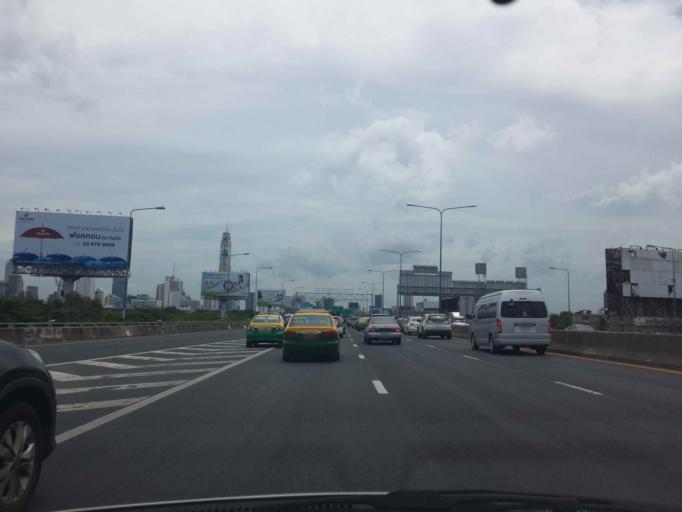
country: TH
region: Bangkok
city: Din Daeng
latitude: 13.7538
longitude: 100.5609
